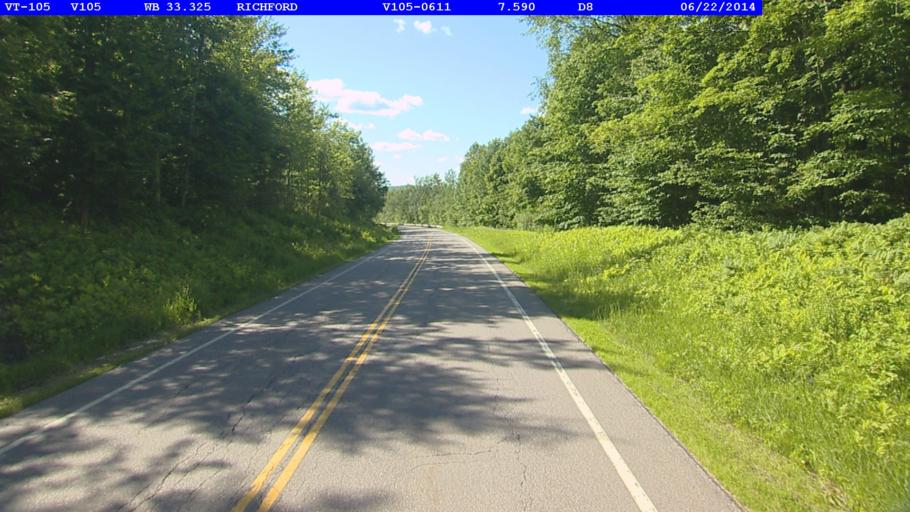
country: US
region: Vermont
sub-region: Franklin County
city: Richford
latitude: 45.0008
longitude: -72.5738
